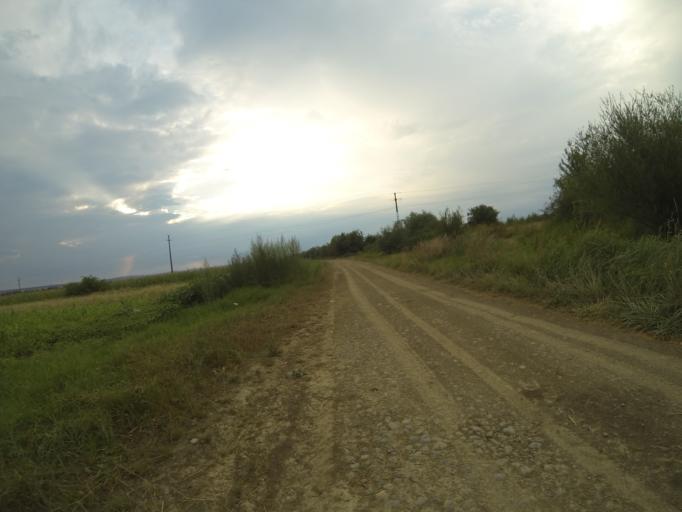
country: RO
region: Brasov
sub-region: Comuna Sinca Veche
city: Sinca Veche
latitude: 45.7710
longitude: 25.1721
